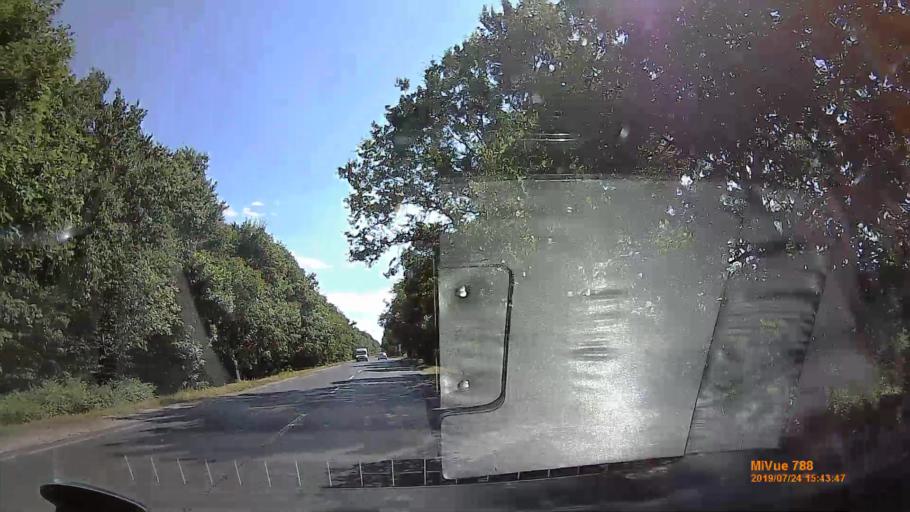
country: HU
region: Szabolcs-Szatmar-Bereg
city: Vasarosnameny
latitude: 48.1077
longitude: 22.3029
